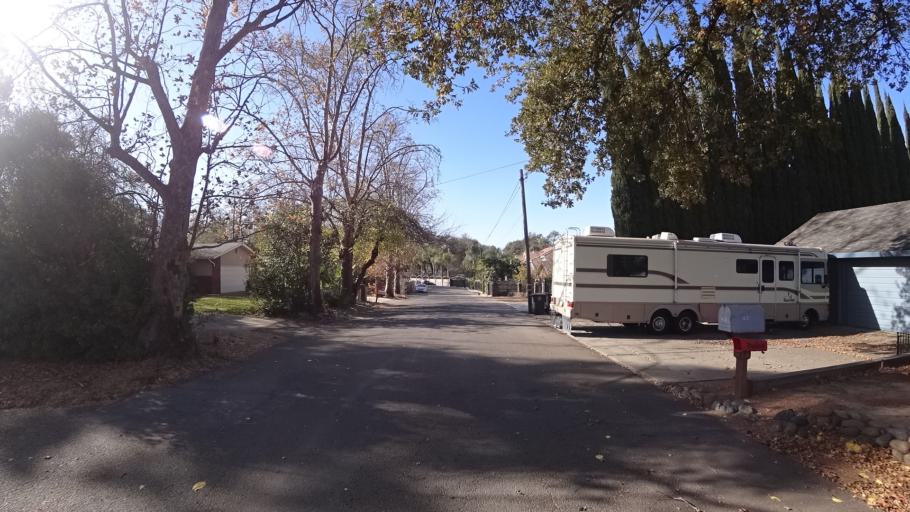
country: US
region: California
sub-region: Sacramento County
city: Citrus Heights
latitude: 38.7065
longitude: -121.2874
